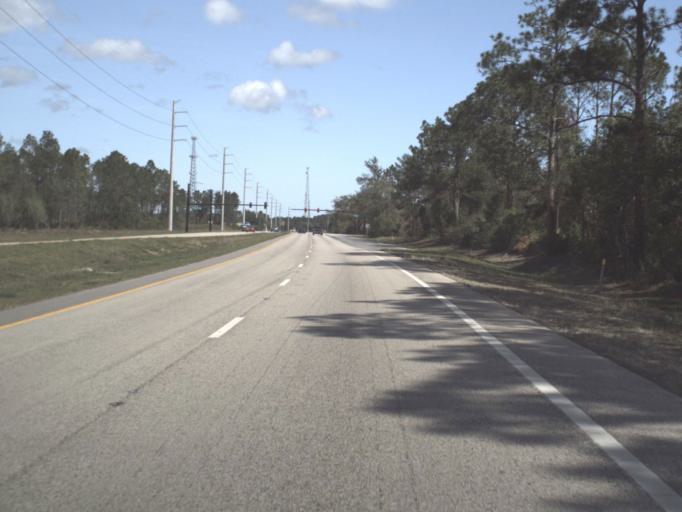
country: US
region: Florida
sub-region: Flagler County
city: Bunnell
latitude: 29.5202
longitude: -81.2626
